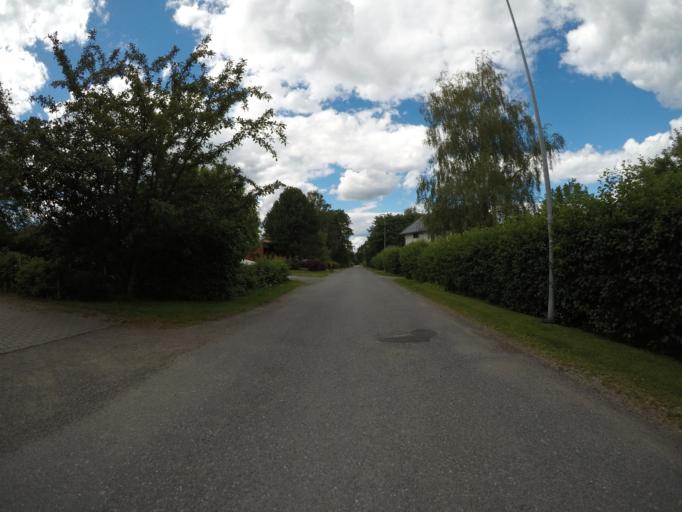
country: FI
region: Haeme
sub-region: Haemeenlinna
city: Haemeenlinna
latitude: 60.9961
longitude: 24.4353
